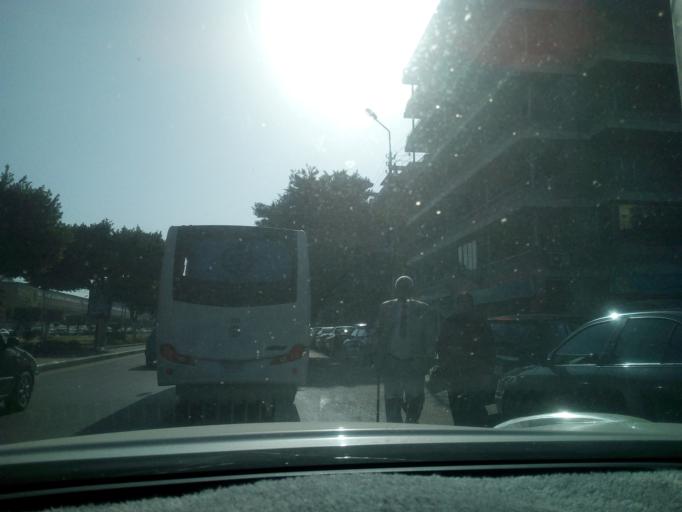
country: EG
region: Muhafazat al Qahirah
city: Cairo
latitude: 30.1031
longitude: 31.3292
